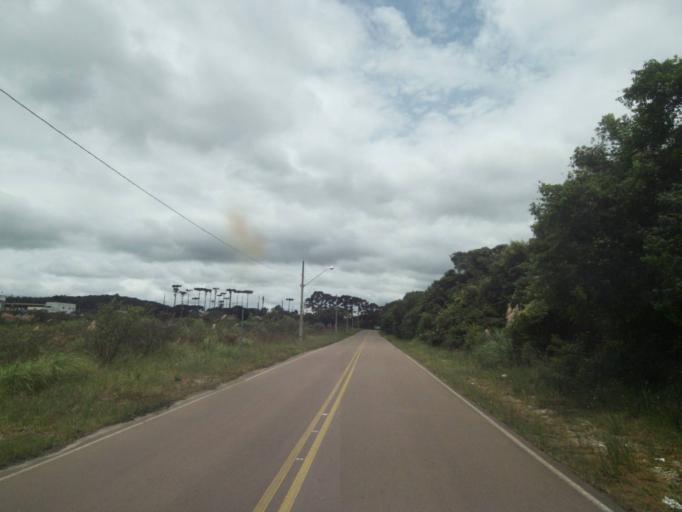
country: BR
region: Parana
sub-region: Campina Grande Do Sul
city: Campina Grande do Sul
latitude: -25.3129
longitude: -49.0195
